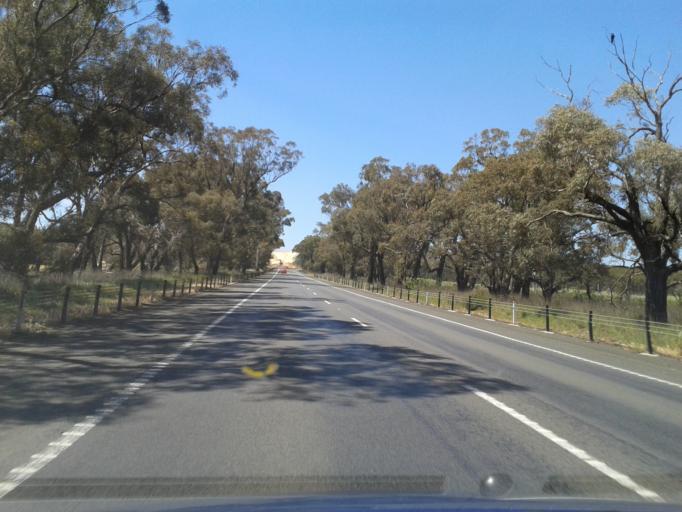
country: AU
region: Victoria
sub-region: Ararat
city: Ararat
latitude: -37.4108
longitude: 143.3199
